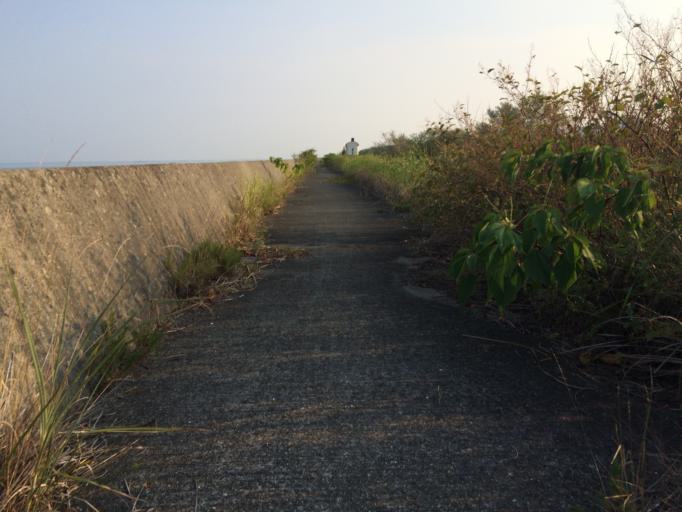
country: JP
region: Yamaguchi
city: Ogori-shimogo
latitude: 34.0145
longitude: 131.3806
